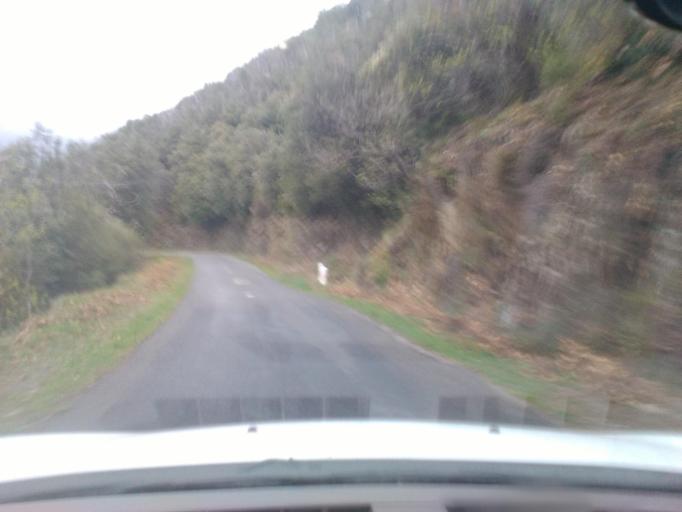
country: FR
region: Languedoc-Roussillon
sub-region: Departement du Gard
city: Valleraugue
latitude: 44.0975
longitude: 3.6459
